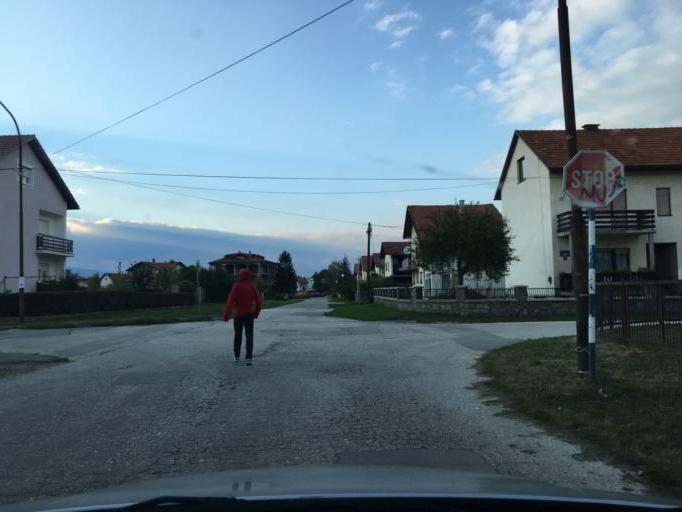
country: BA
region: Federation of Bosnia and Herzegovina
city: Bugojno
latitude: 44.0623
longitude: 17.4523
